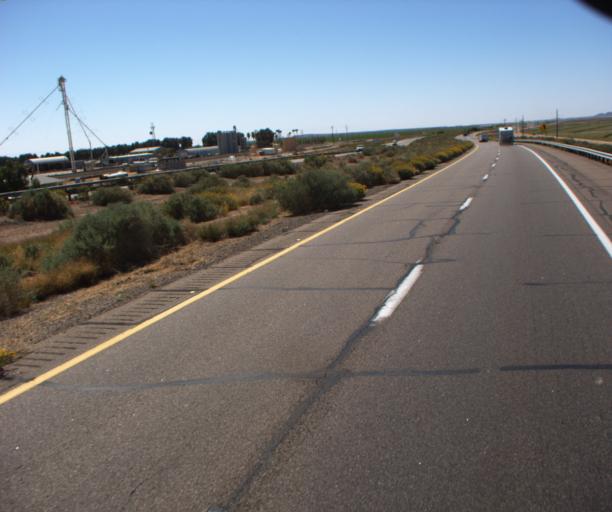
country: US
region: Arizona
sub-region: Maricopa County
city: Gila Bend
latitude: 32.9218
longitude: -112.8887
